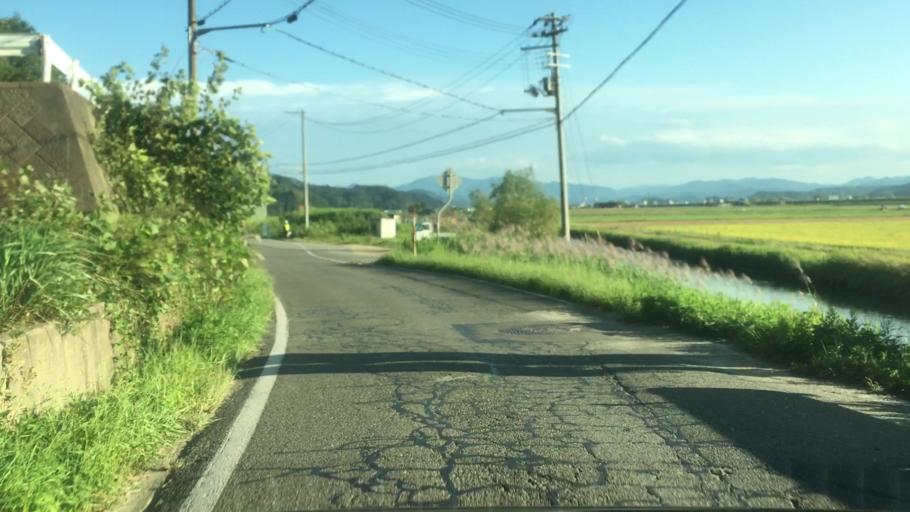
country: JP
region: Hyogo
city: Toyooka
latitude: 35.5870
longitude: 134.8050
